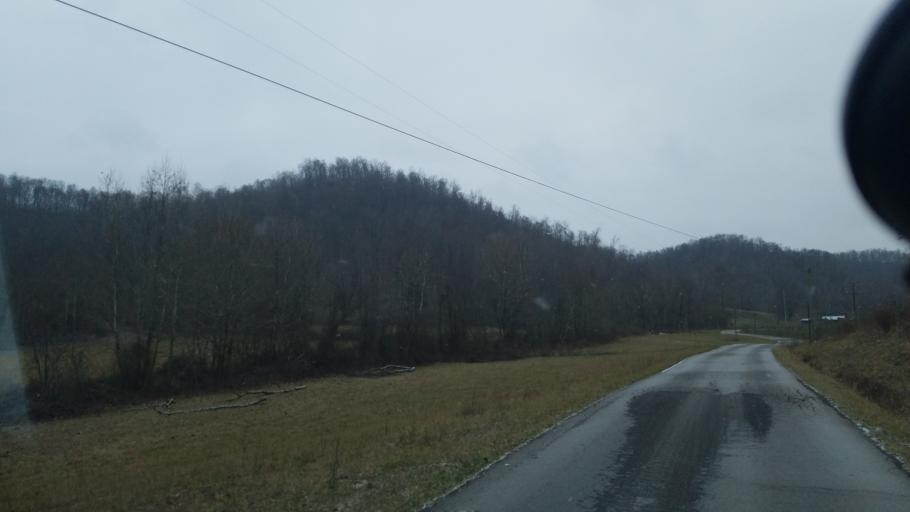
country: US
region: Kentucky
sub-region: Lewis County
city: Vanceburg
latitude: 38.4838
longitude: -83.4941
